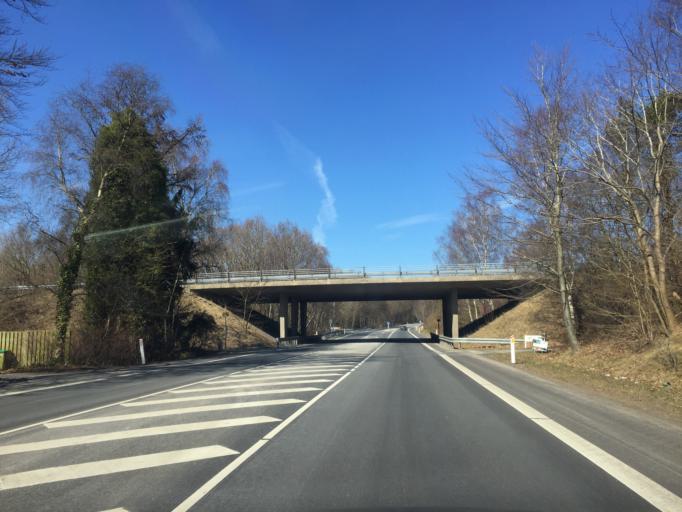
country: DK
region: Capital Region
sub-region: Fredensborg Kommune
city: Humlebaek
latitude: 55.9951
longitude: 12.4871
